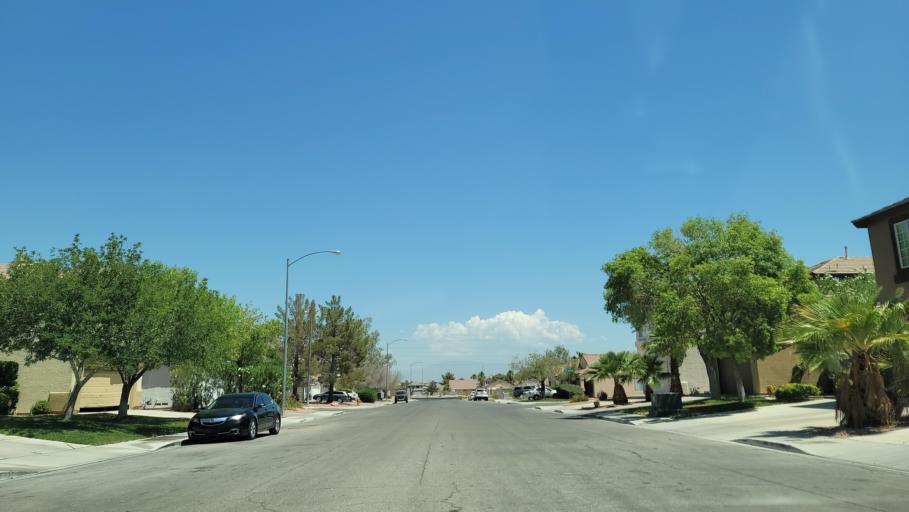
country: US
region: Nevada
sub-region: Clark County
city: Spring Valley
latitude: 36.0831
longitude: -115.2565
